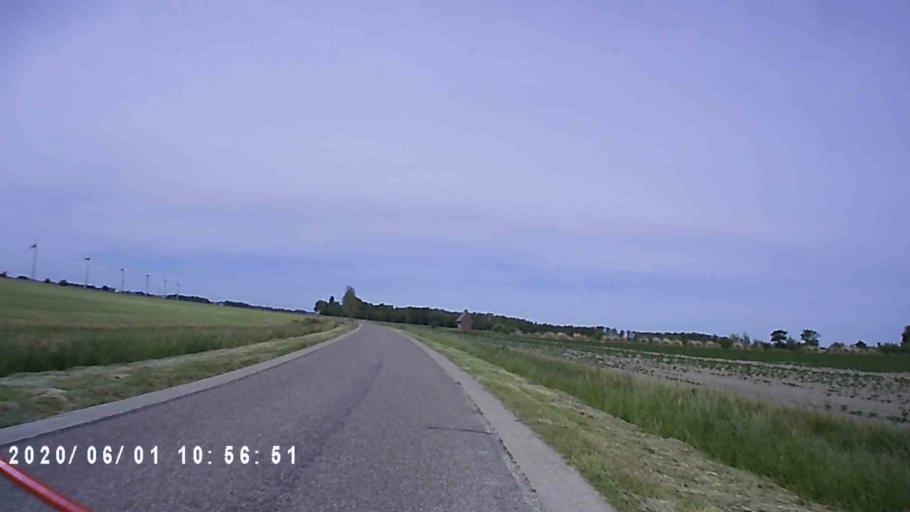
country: NL
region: Friesland
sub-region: Gemeente Franekeradeel
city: Sexbierum
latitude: 53.1993
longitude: 5.4952
